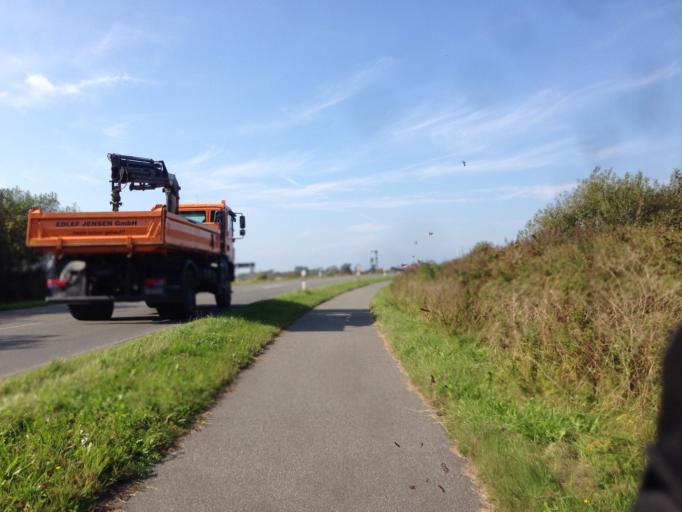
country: DE
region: Schleswig-Holstein
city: Keitum
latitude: 54.8912
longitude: 8.3611
